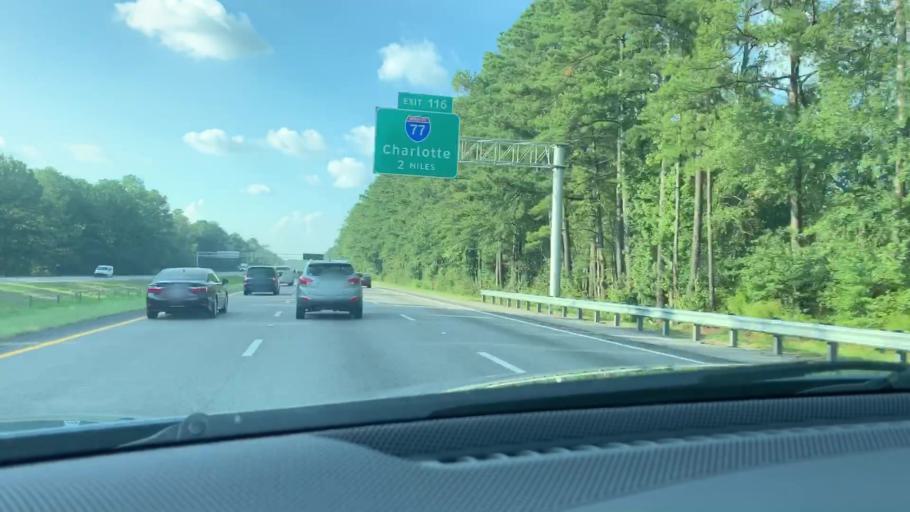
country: US
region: South Carolina
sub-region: Lexington County
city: Pineridge
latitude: 33.8967
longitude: -81.0452
